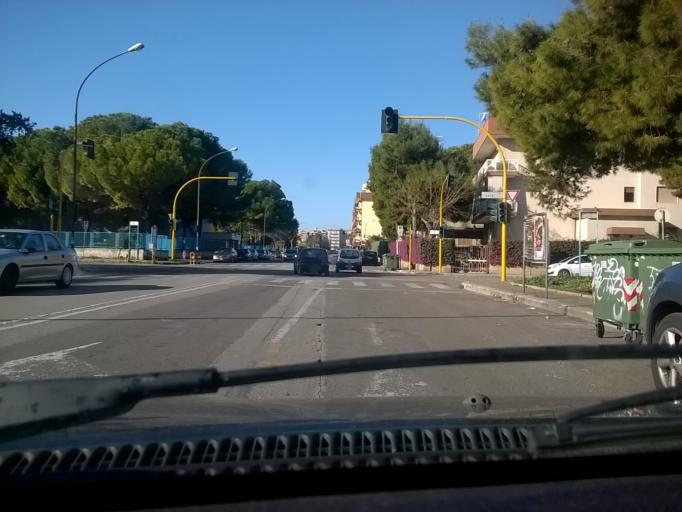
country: IT
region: Apulia
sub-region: Provincia di Taranto
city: Taranto
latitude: 40.4611
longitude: 17.2655
